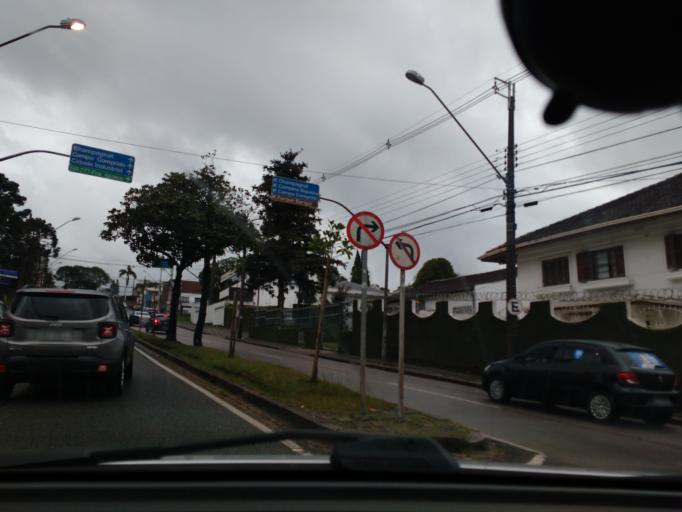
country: BR
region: Parana
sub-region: Curitiba
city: Curitiba
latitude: -25.4230
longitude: -49.2784
